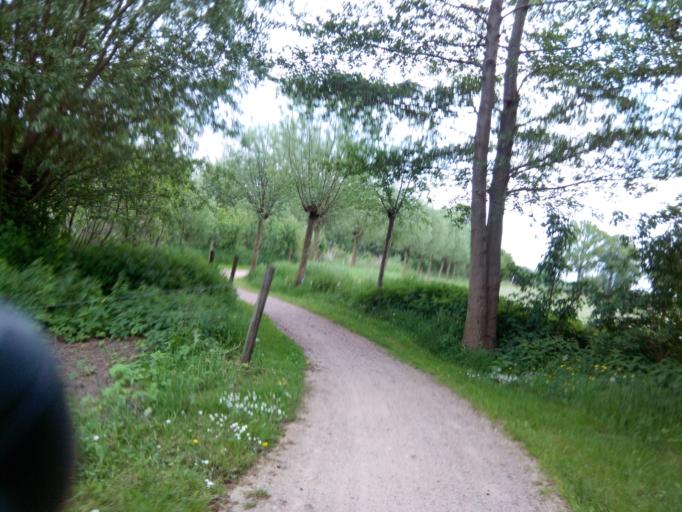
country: NL
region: Gelderland
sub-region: Berkelland
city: Borculo
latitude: 52.0784
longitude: 6.5759
